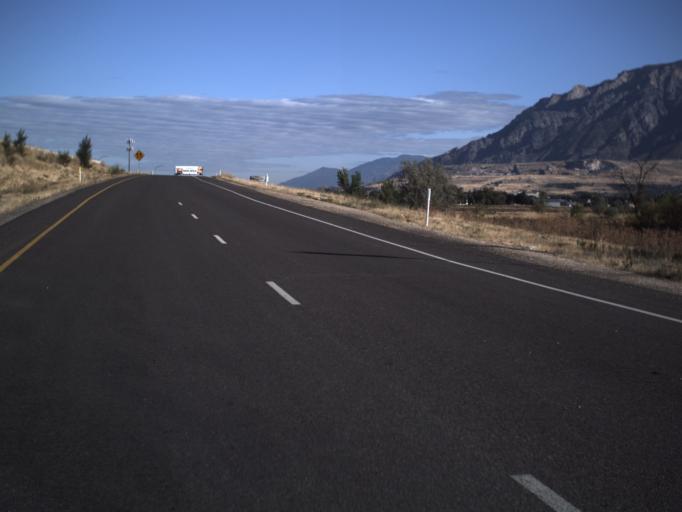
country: US
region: Utah
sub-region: Weber County
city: Marriott-Slaterville
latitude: 41.2686
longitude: -112.0256
